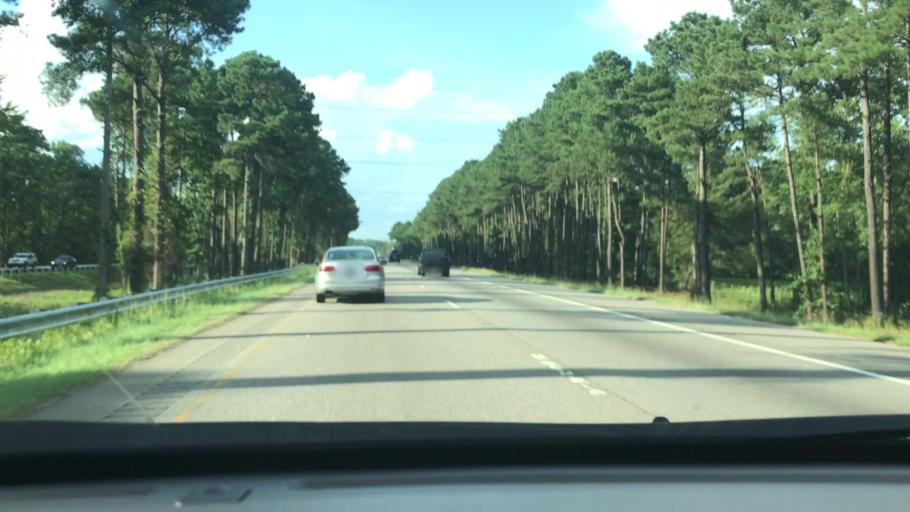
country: US
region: North Carolina
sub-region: Robeson County
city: Lumberton
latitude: 34.6870
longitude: -79.0003
